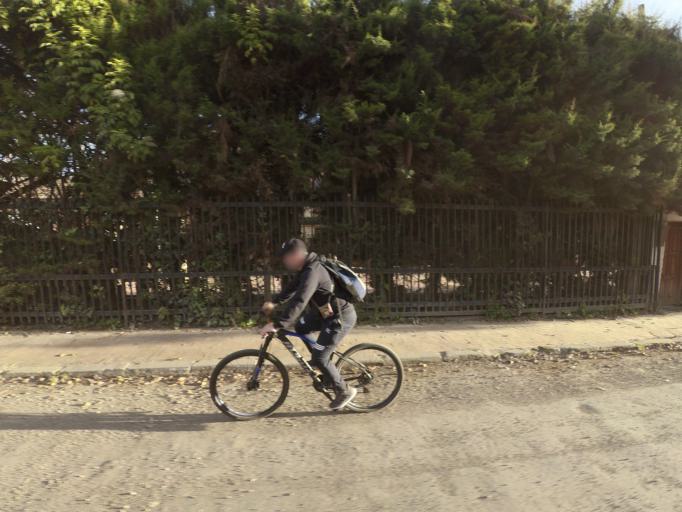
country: CO
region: Cundinamarca
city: Chia
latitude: 4.8402
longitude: -74.0304
